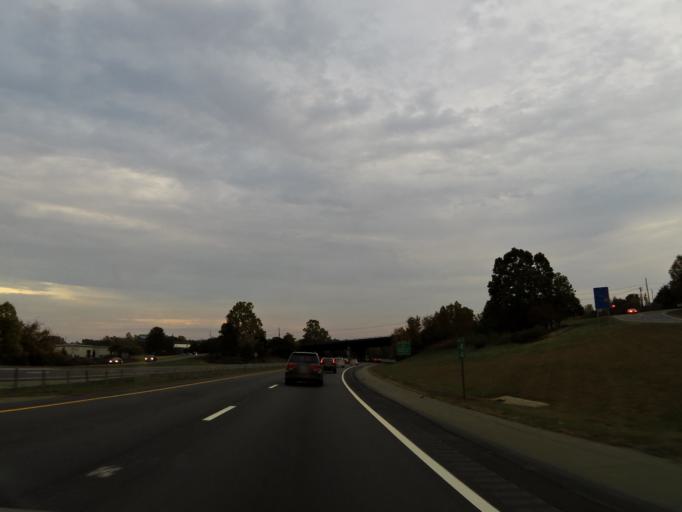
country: US
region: North Carolina
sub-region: Catawba County
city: Hickory
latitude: 35.7241
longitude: -81.3571
